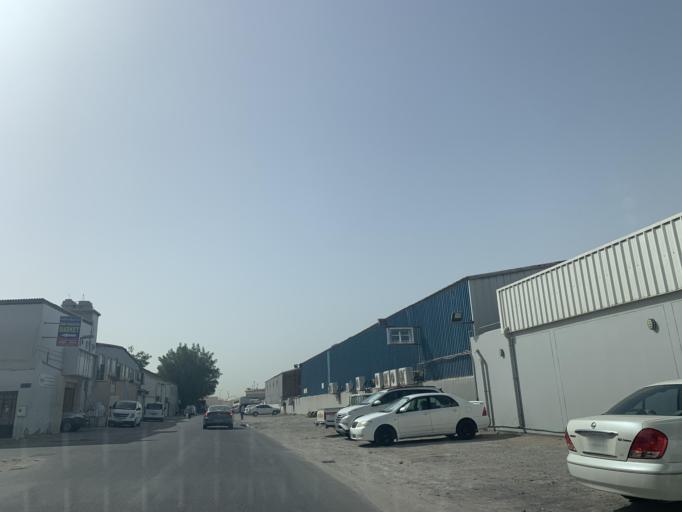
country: BH
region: Northern
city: Sitrah
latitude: 26.1533
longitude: 50.6181
